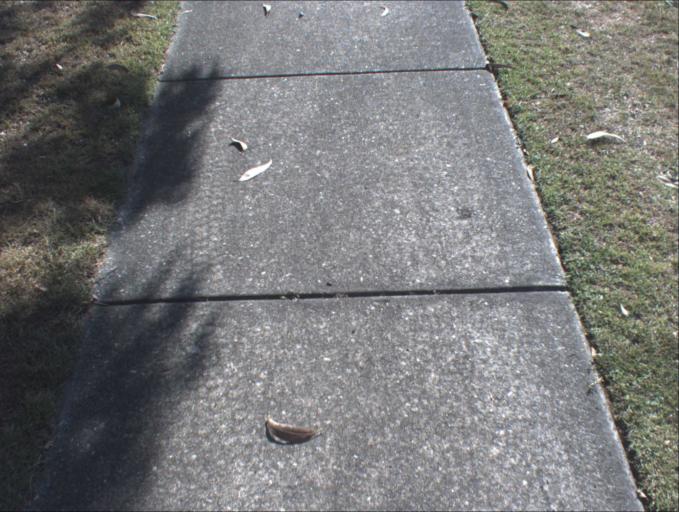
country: AU
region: Queensland
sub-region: Logan
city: Beenleigh
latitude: -27.7161
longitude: 153.1830
